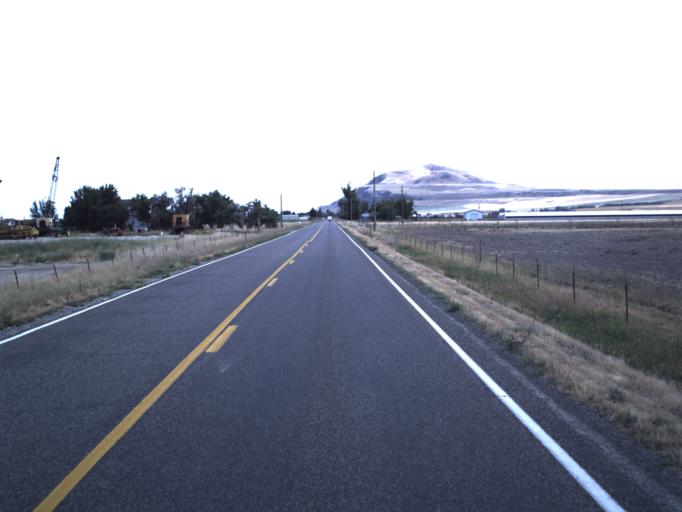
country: US
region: Utah
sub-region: Cache County
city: Lewiston
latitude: 41.9555
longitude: -111.9540
